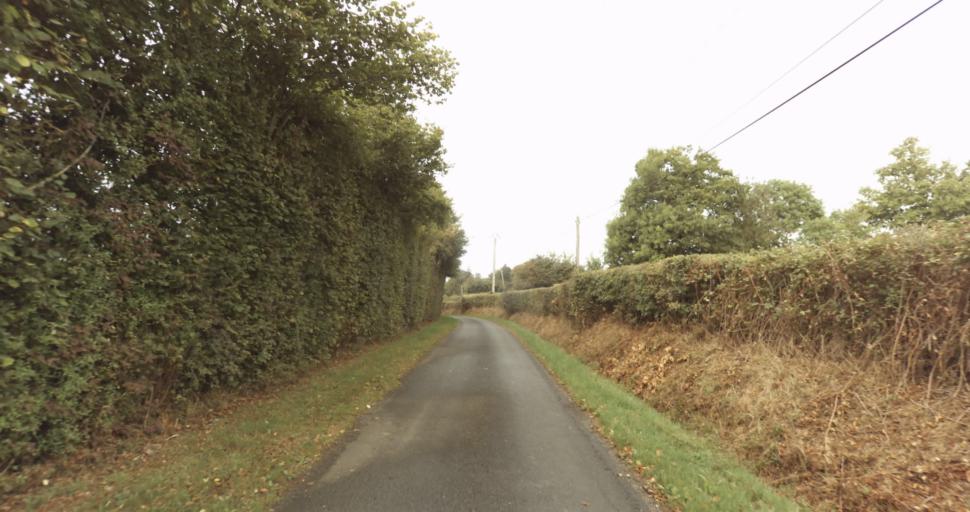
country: FR
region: Lower Normandy
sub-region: Departement de l'Orne
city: Aube-sur-Rile
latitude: 48.7364
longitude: 0.4905
